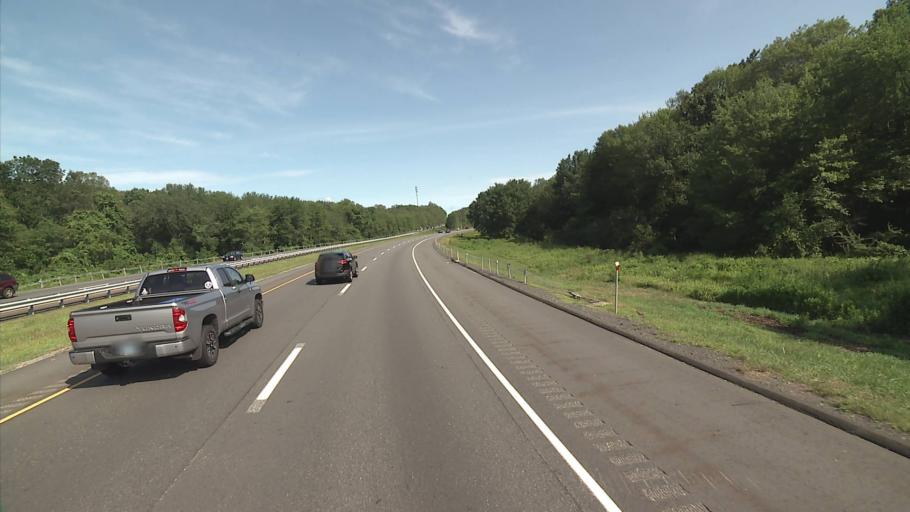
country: US
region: Connecticut
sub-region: Hartford County
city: Terramuggus
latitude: 41.6106
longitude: -72.4331
